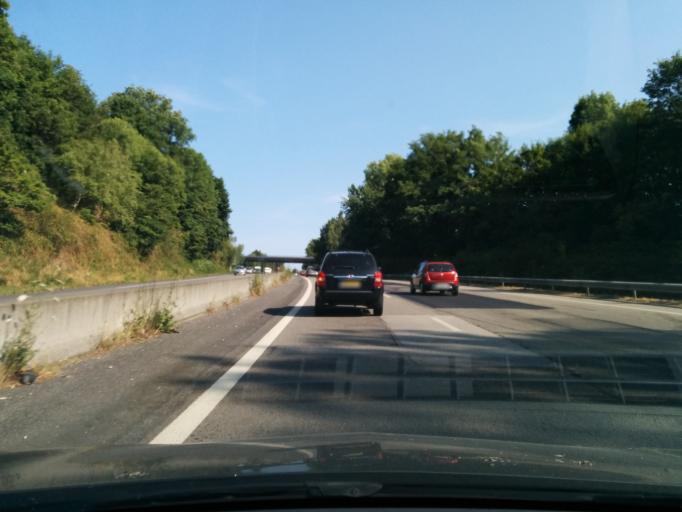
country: FR
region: Limousin
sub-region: Departement de la Haute-Vienne
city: Condat-sur-Vienne
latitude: 45.7966
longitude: 1.2976
